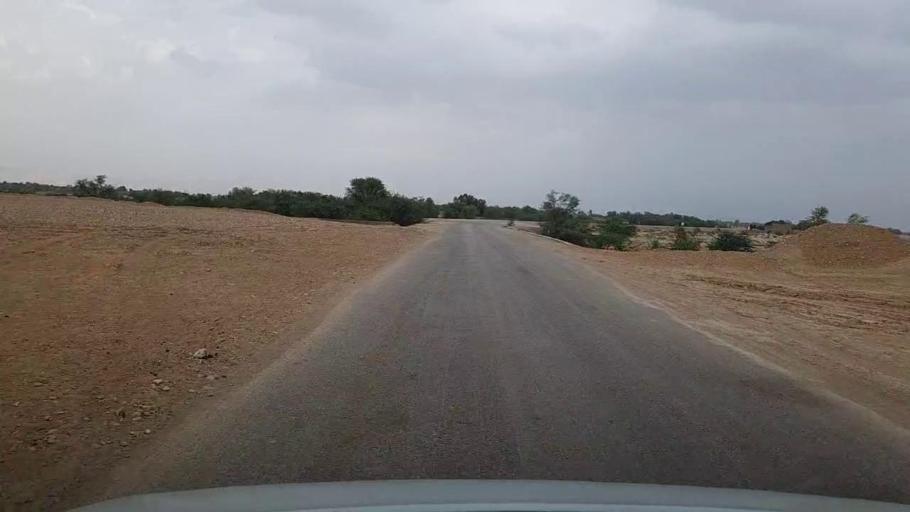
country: PK
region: Sindh
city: Sehwan
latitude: 26.3388
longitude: 67.7270
